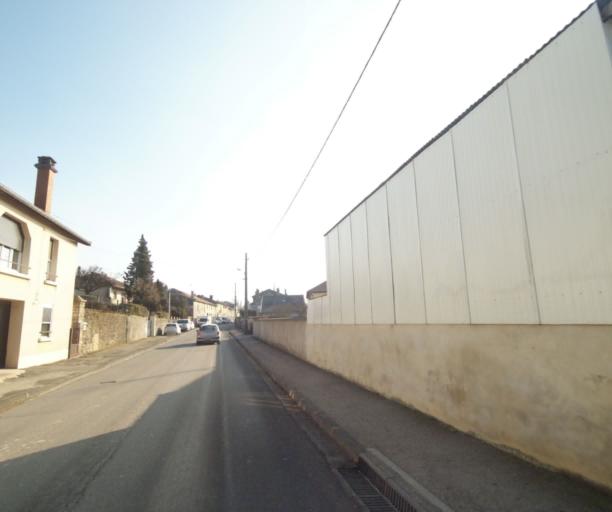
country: FR
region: Champagne-Ardenne
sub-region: Departement de la Haute-Marne
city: Wassy
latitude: 48.5028
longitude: 4.9450
